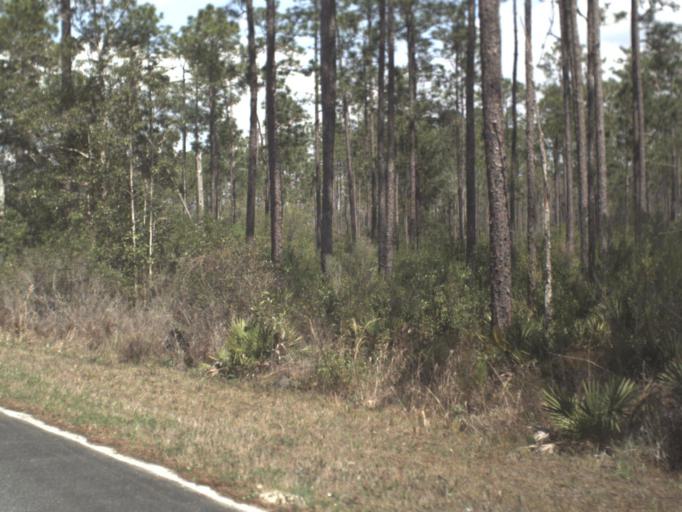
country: US
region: Florida
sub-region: Gulf County
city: Wewahitchka
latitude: 29.9935
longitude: -84.9768
